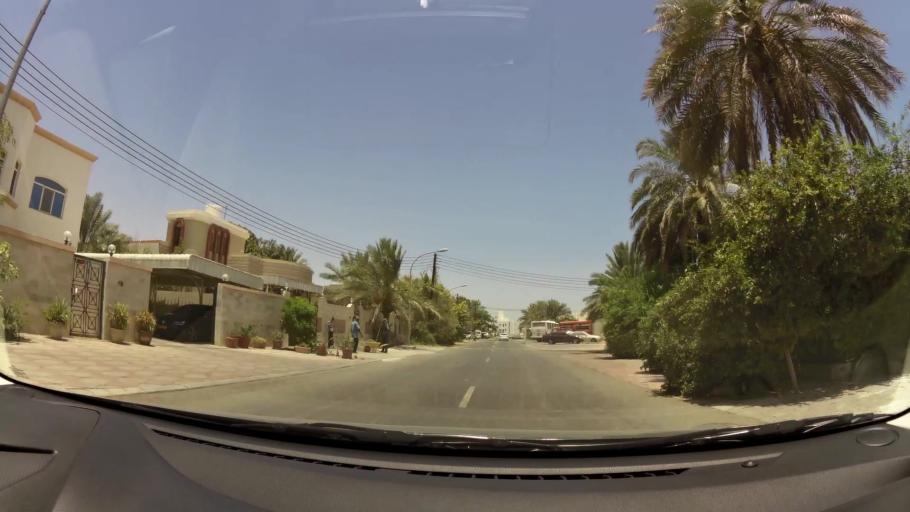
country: OM
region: Muhafazat Masqat
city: As Sib al Jadidah
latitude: 23.6366
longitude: 58.2346
